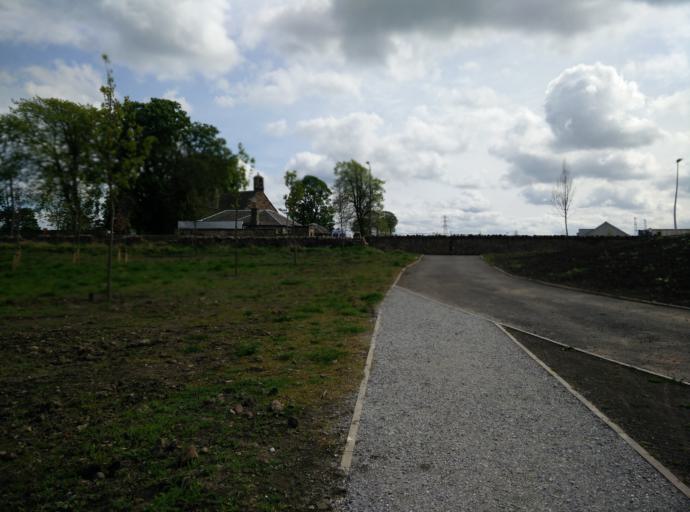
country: GB
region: Scotland
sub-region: Midlothian
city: Dalkeith
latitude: 55.9126
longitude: -3.0988
